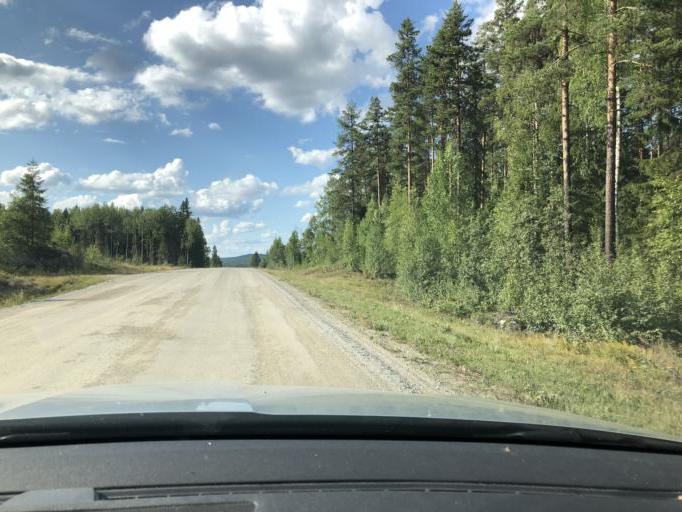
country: SE
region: Vaesternorrland
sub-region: Solleftea Kommun
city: Solleftea
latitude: 63.3156
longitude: 17.2461
